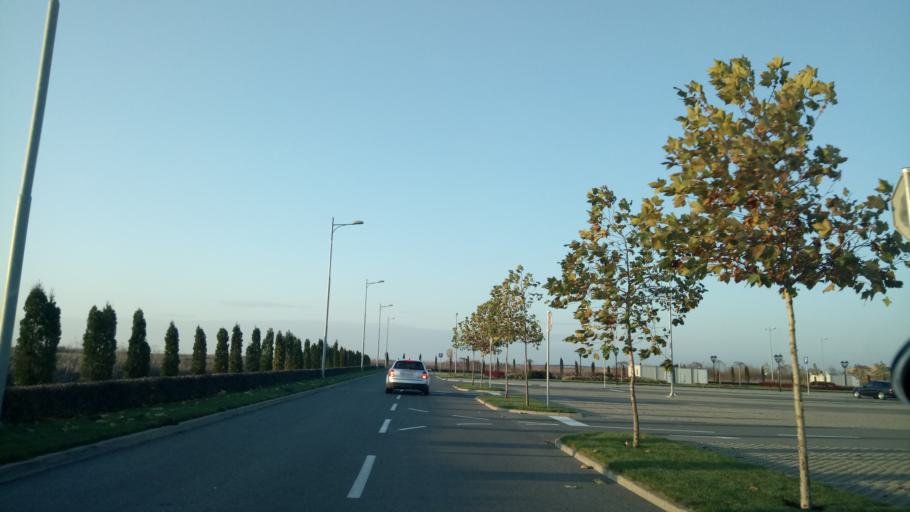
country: RS
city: Novi Karlovci
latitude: 45.0691
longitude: 20.1347
